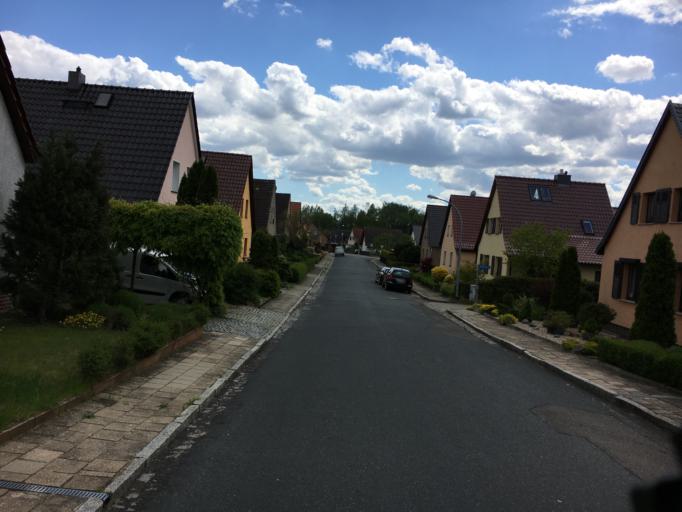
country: DE
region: Brandenburg
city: Juterbog
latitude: 52.0016
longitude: 13.0912
